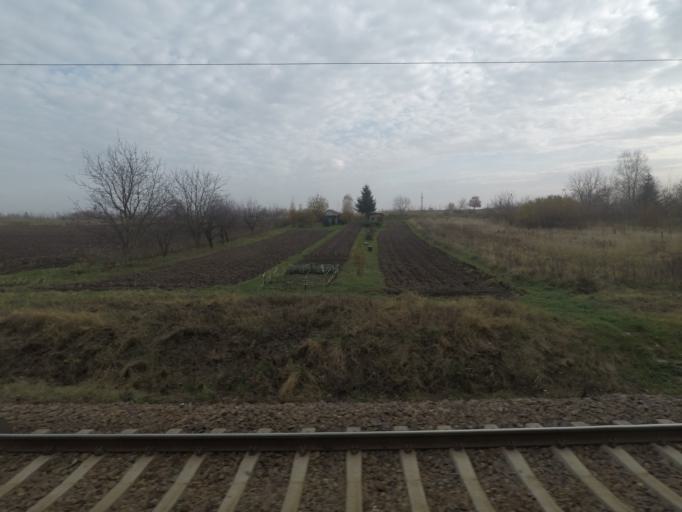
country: PL
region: Subcarpathian Voivodeship
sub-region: Powiat przemyski
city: Zurawica
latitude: 49.8151
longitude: 22.8099
